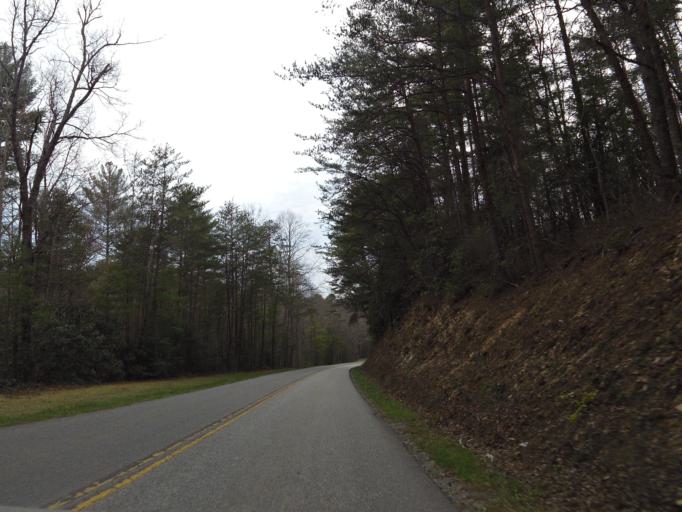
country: US
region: Tennessee
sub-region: Blount County
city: Wildwood
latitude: 35.6045
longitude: -83.7649
